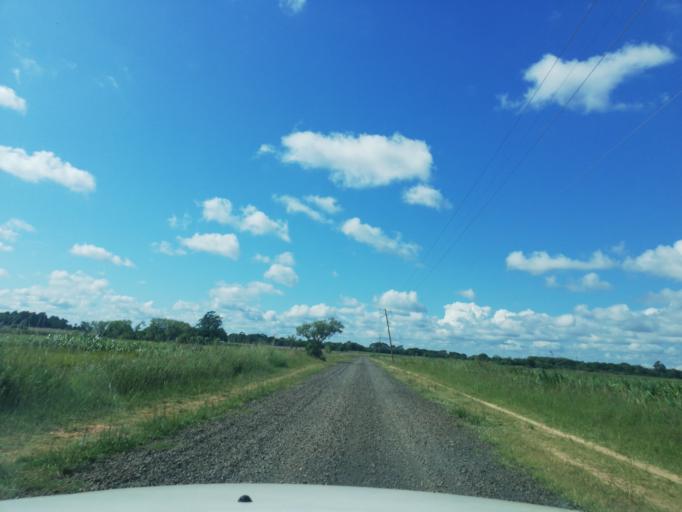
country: AR
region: Corrientes
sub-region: Departamento de San Miguel
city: San Miguel
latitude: -27.9779
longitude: -57.5808
